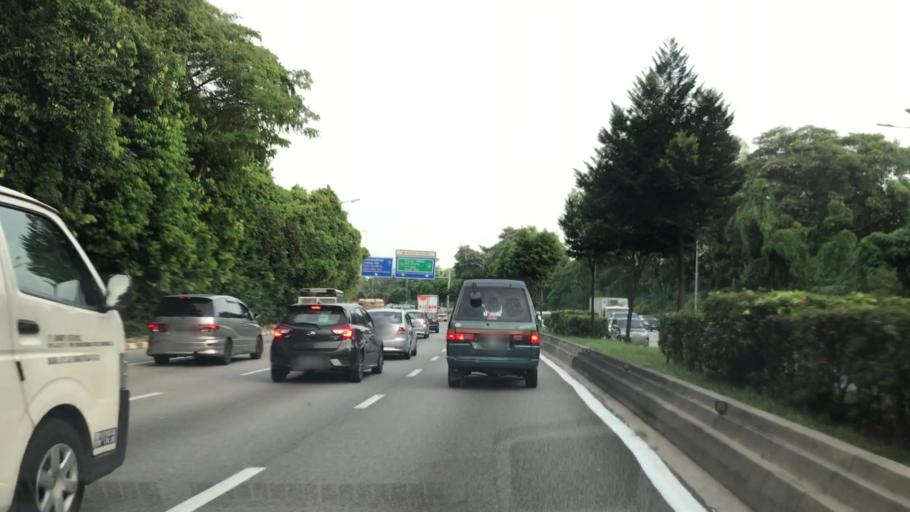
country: MY
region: Kuala Lumpur
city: Kuala Lumpur
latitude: 3.1259
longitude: 101.7025
